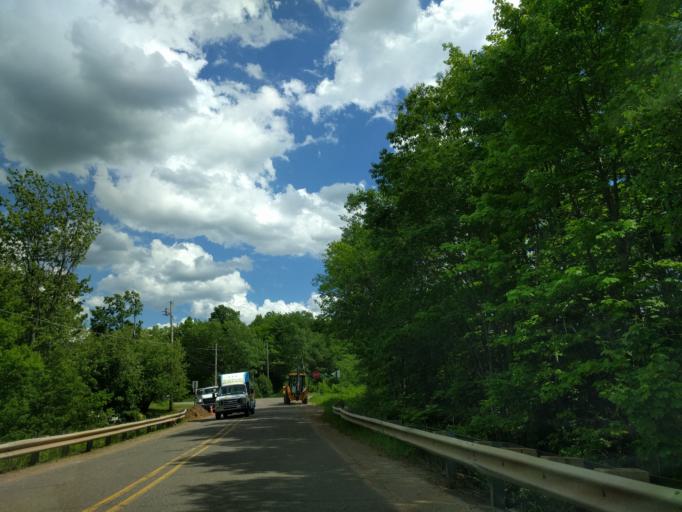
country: US
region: Michigan
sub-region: Marquette County
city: Trowbridge Park
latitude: 46.5413
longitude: -87.5136
